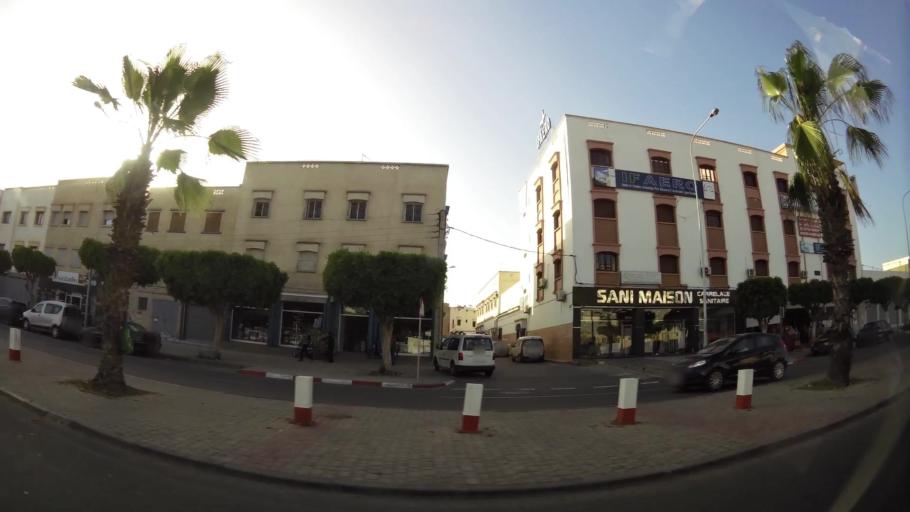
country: MA
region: Oued ed Dahab-Lagouira
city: Dakhla
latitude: 30.4107
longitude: -9.5475
